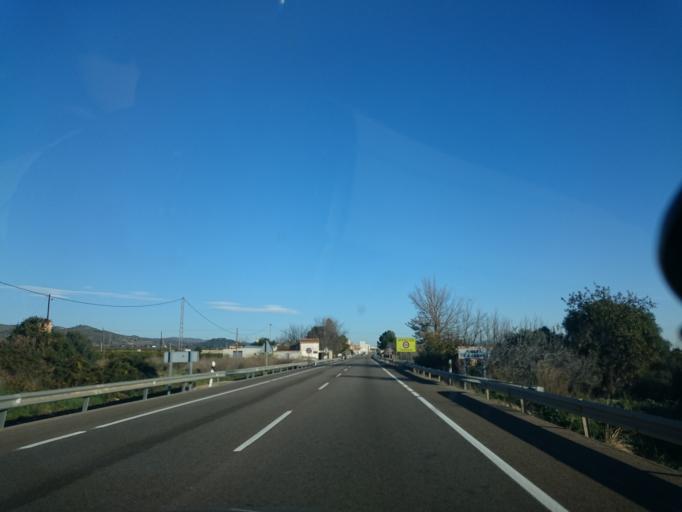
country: ES
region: Valencia
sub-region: Provincia de Castello
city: Orpesa/Oropesa del Mar
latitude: 40.1478
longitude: 0.1558
